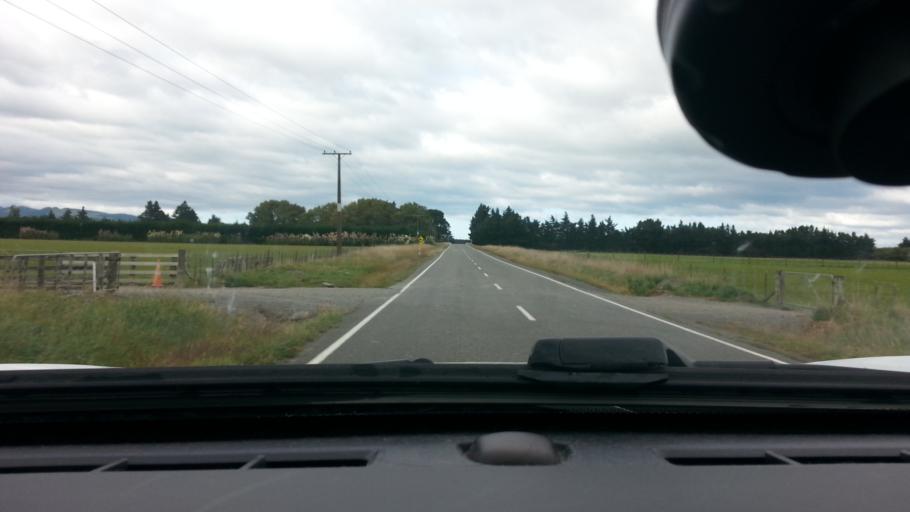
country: NZ
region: Wellington
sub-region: Upper Hutt City
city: Upper Hutt
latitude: -41.3390
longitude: 175.2098
